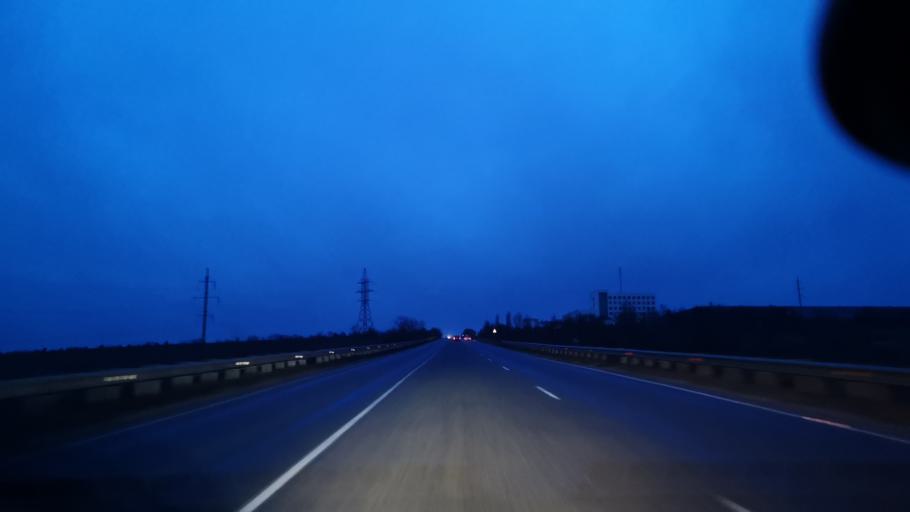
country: MD
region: Orhei
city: Orhei
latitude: 47.3948
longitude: 28.7991
